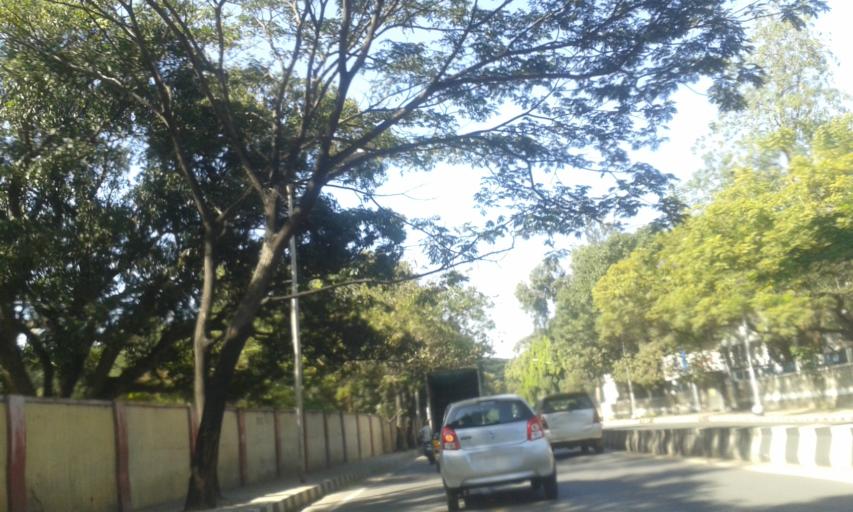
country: IN
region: Karnataka
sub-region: Bangalore Urban
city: Bangalore
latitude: 12.9635
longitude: 77.6264
